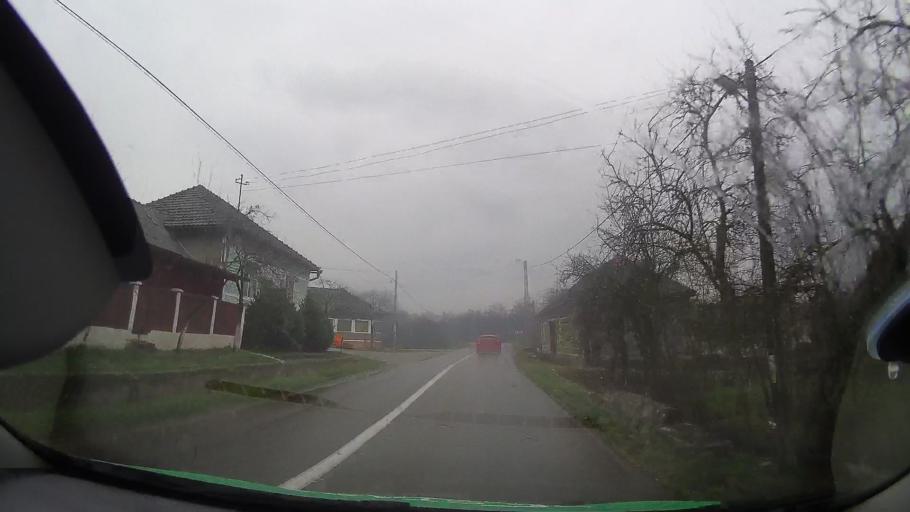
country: RO
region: Bihor
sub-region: Comuna Holod
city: Vintere
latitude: 46.7716
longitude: 22.1376
